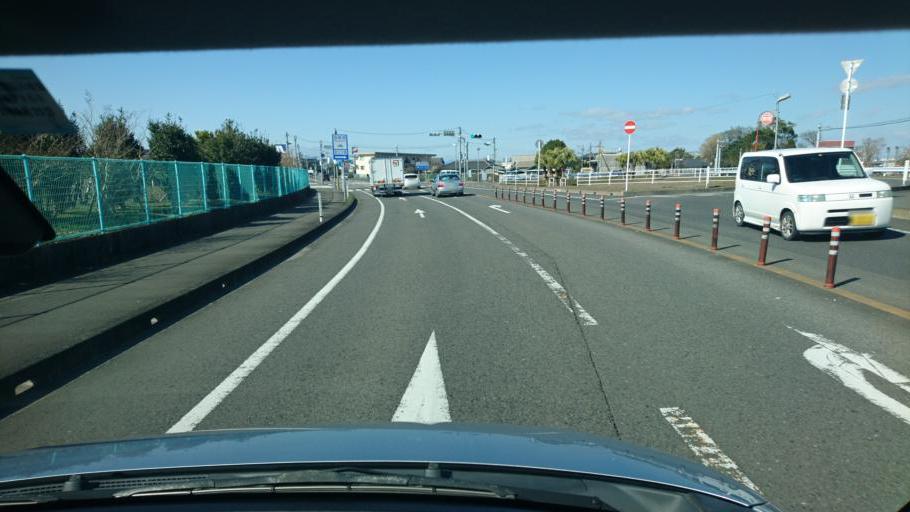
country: JP
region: Miyazaki
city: Miyazaki-shi
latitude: 31.8742
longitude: 131.4308
